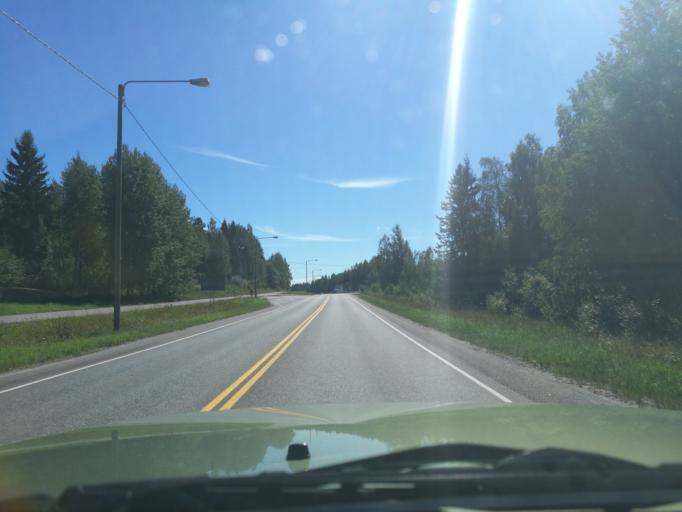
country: FI
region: Uusimaa
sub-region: Helsinki
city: Kerava
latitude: 60.3576
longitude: 25.1274
